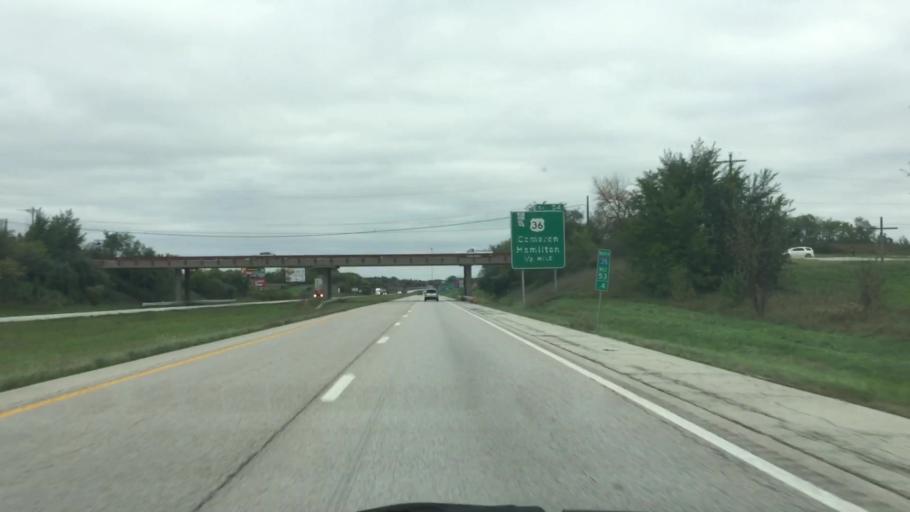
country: US
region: Missouri
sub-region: Clinton County
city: Cameron
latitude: 39.7414
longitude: -94.2201
